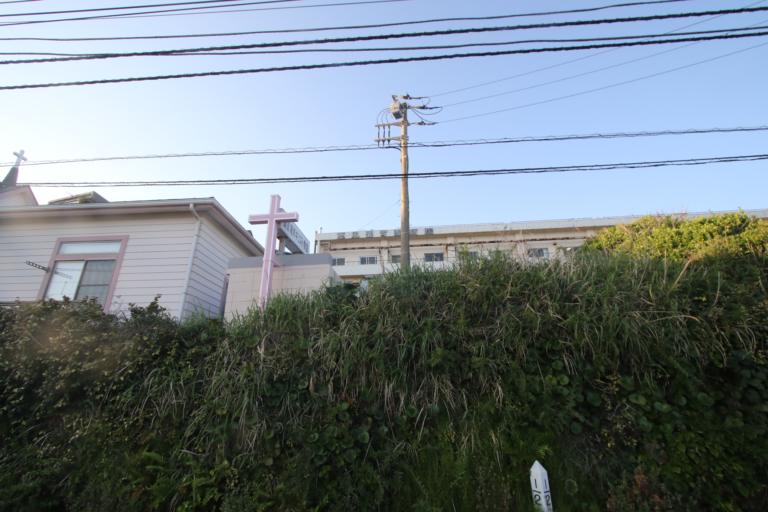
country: JP
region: Kanagawa
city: Fujisawa
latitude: 35.3068
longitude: 139.4973
